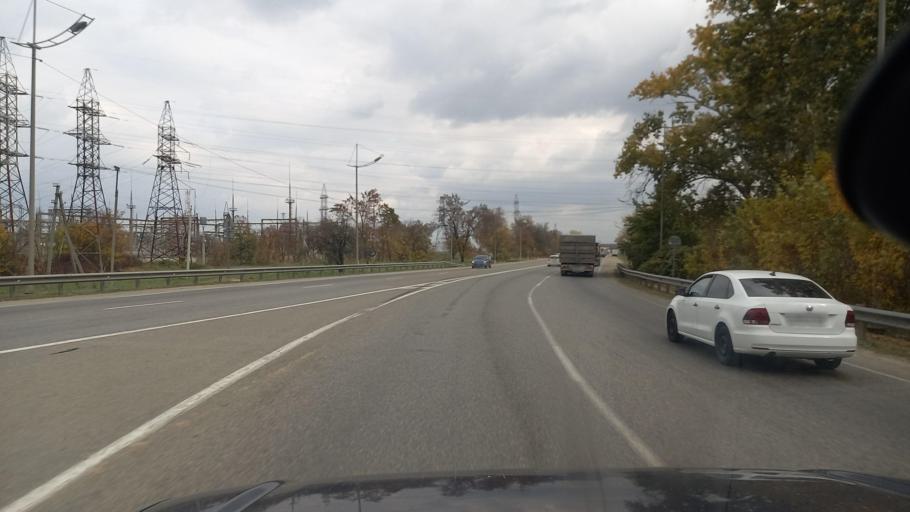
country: RU
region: Krasnodarskiy
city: Afipskiy
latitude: 44.8860
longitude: 38.8445
